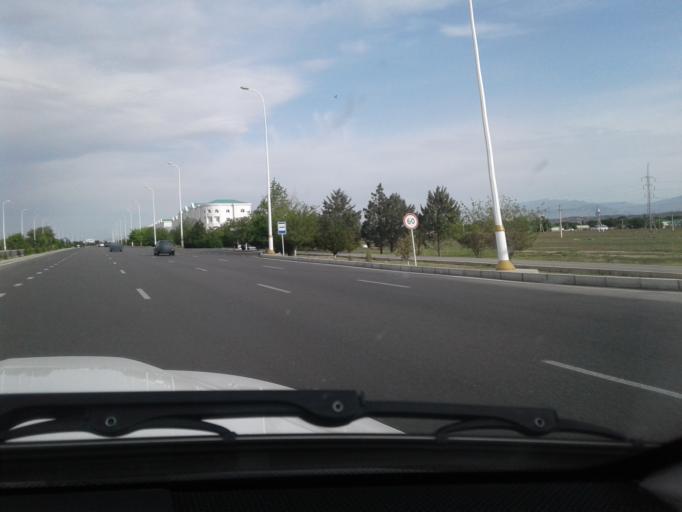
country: TM
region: Ahal
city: Ashgabat
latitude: 37.9954
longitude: 58.3096
